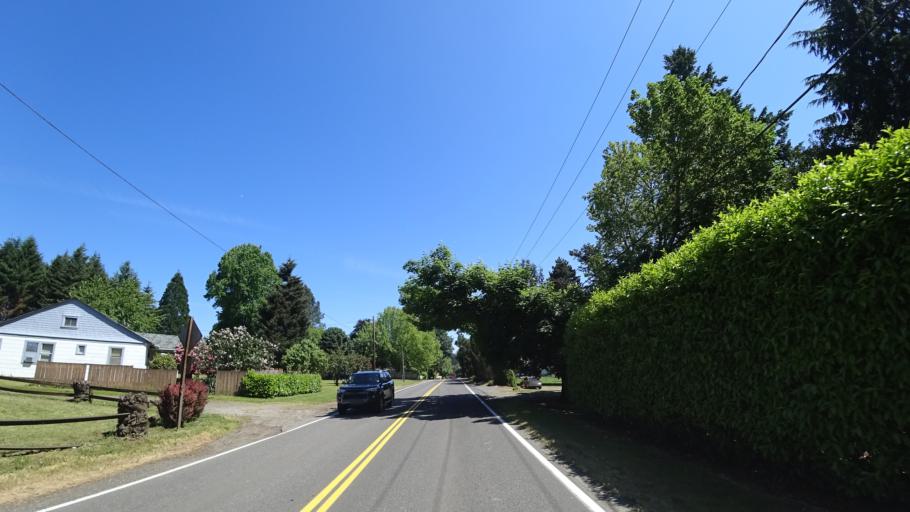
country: US
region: Oregon
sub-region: Clackamas County
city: Happy Valley
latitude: 45.4707
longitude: -122.4917
